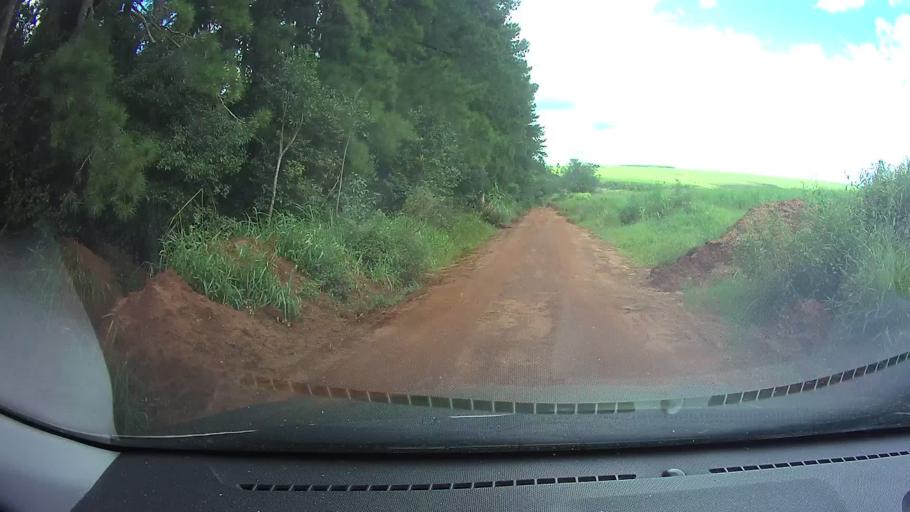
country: PY
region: Paraguari
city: La Colmena
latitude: -25.9524
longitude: -56.7733
